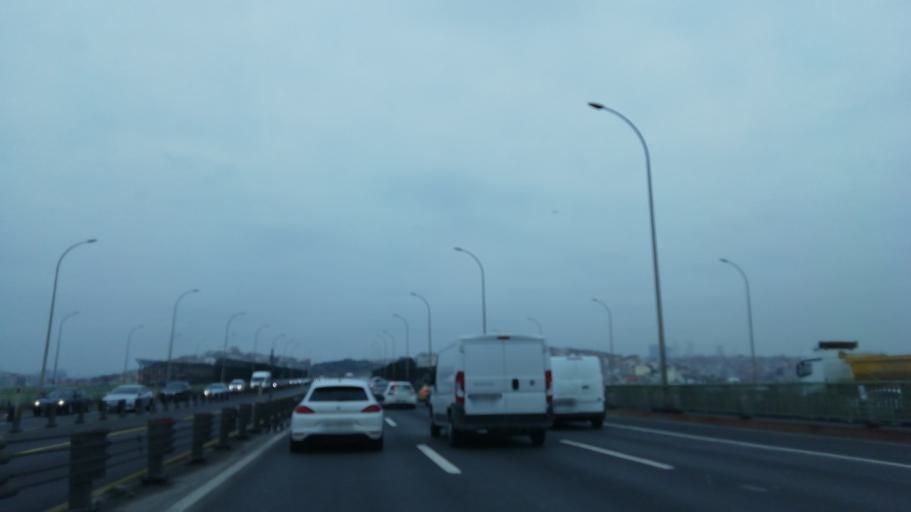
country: TR
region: Istanbul
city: Istanbul
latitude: 41.0400
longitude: 28.9390
